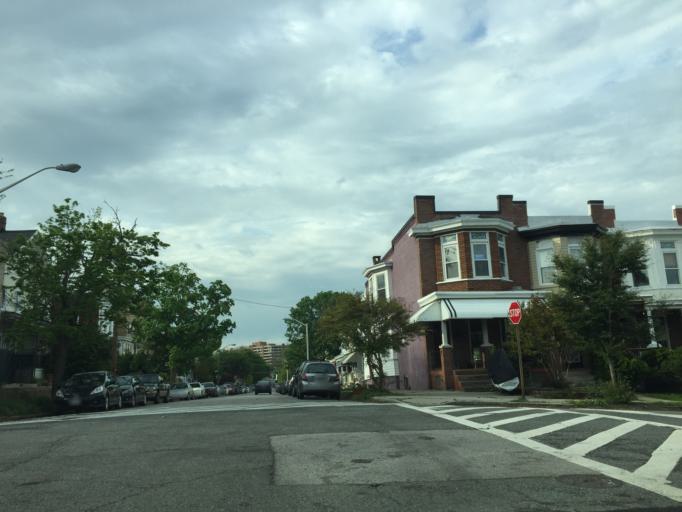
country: US
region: Maryland
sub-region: City of Baltimore
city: Baltimore
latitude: 39.3325
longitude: -76.6312
